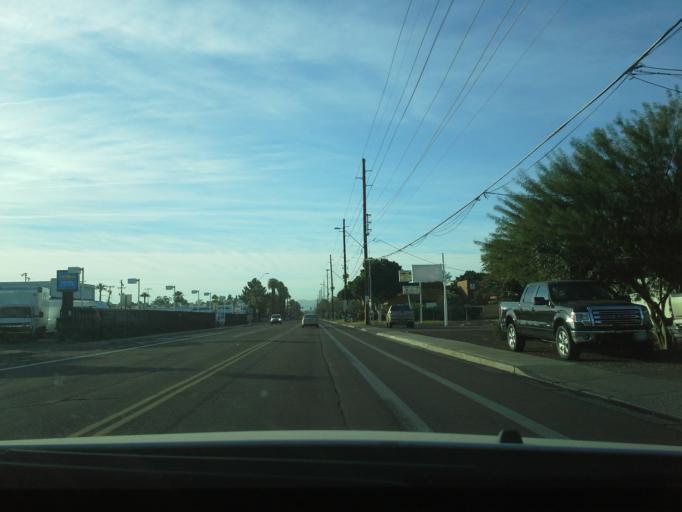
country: US
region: Arizona
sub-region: Maricopa County
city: Phoenix
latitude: 33.5089
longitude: -112.0563
